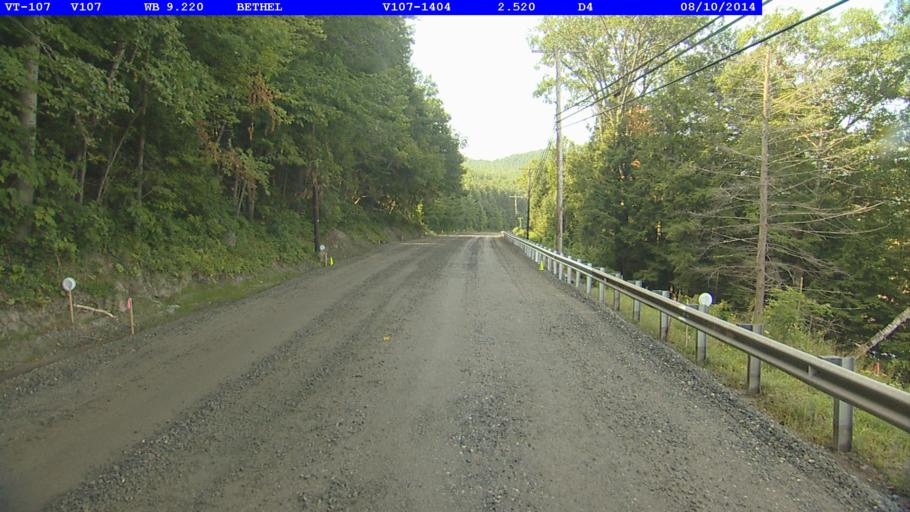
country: US
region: Vermont
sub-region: Orange County
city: Randolph
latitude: 43.8170
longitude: -72.6356
